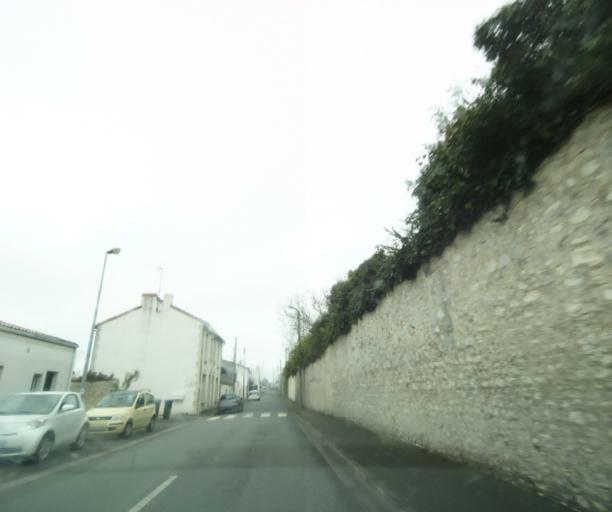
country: FR
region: Poitou-Charentes
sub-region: Departement de la Charente-Maritime
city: La Rochelle
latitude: 46.1764
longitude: -1.1410
